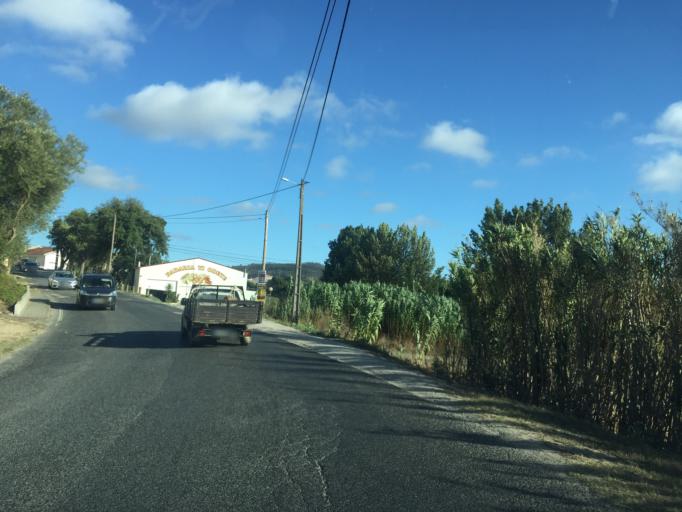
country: PT
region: Lisbon
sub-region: Torres Vedras
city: A dos Cunhados
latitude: 39.1483
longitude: -9.2880
